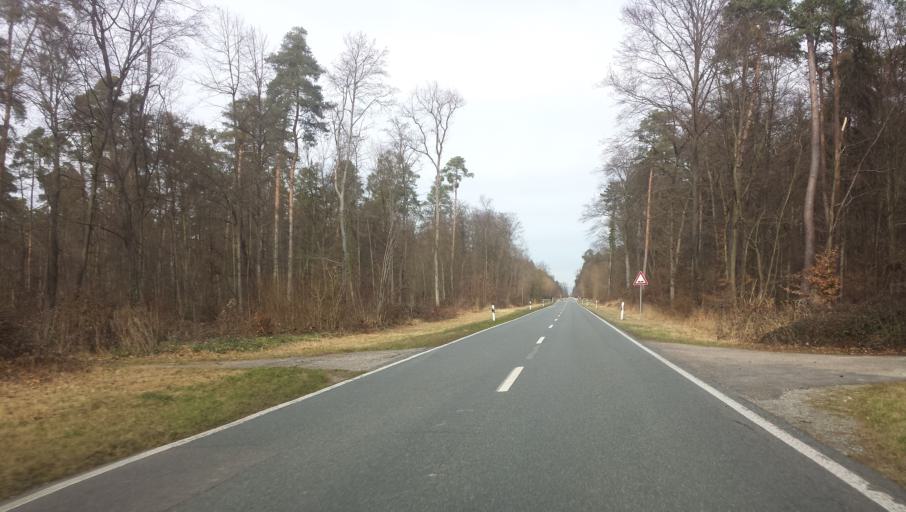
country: DE
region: Baden-Wuerttemberg
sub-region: Karlsruhe Region
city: Reilingen
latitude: 49.2631
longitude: 8.5528
